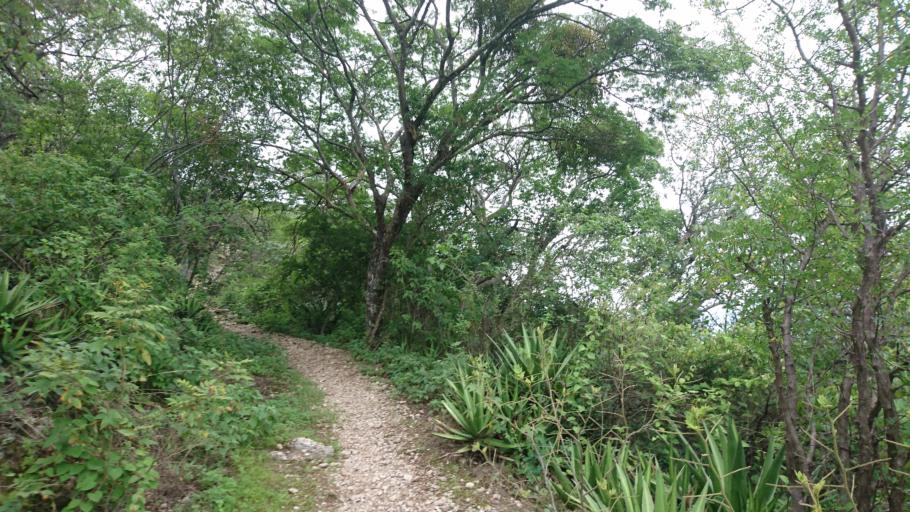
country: MX
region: Oaxaca
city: San Lorenzo Albarradas
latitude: 16.8660
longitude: -96.2743
